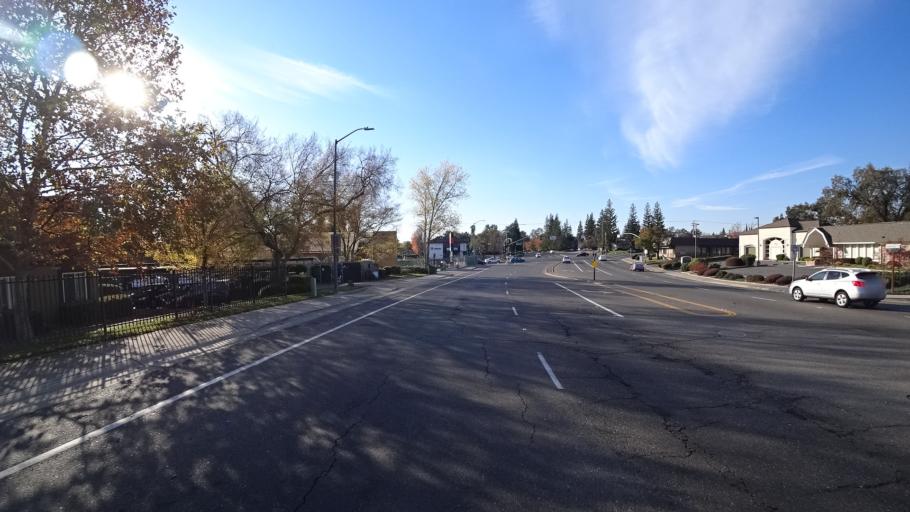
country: US
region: California
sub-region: Sacramento County
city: Foothill Farms
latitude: 38.6617
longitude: -121.3366
